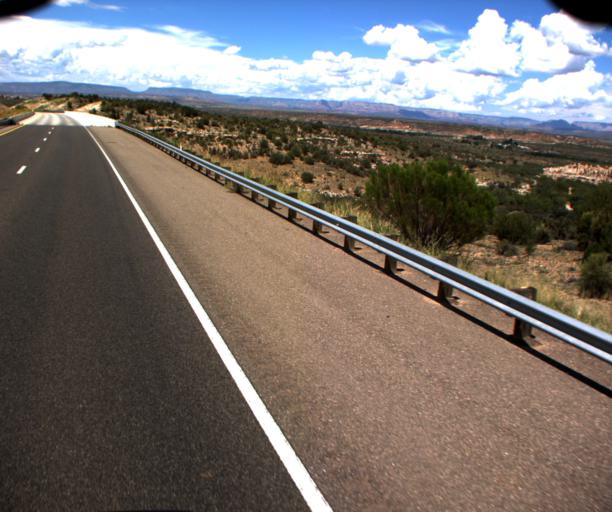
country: US
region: Arizona
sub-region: Yavapai County
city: Verde Village
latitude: 34.6698
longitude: -111.9684
